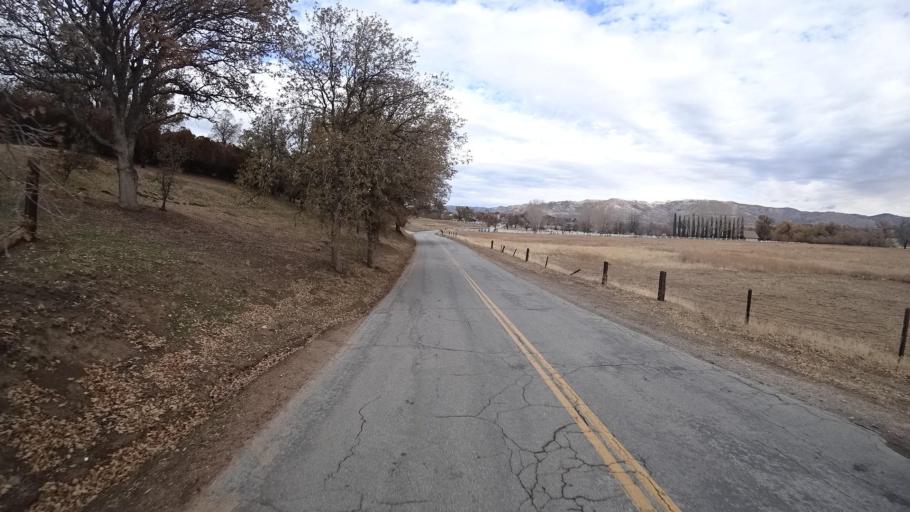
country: US
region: California
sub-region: Kern County
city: Golden Hills
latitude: 35.1328
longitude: -118.5071
